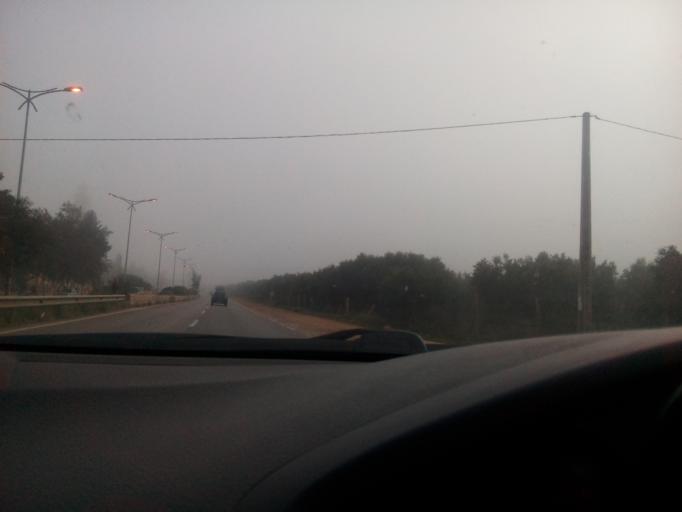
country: DZ
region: Oran
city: Bou Tlelis
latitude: 35.5880
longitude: -0.8064
